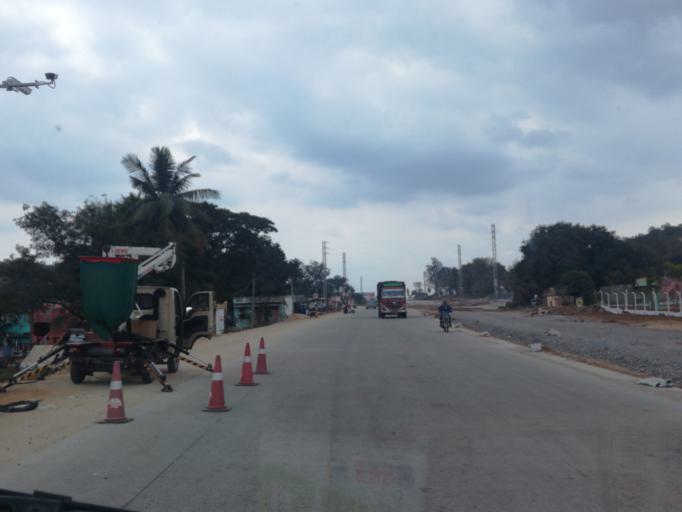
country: IN
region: Andhra Pradesh
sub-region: Chittoor
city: Ramapuram
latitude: 13.0930
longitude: 79.1336
